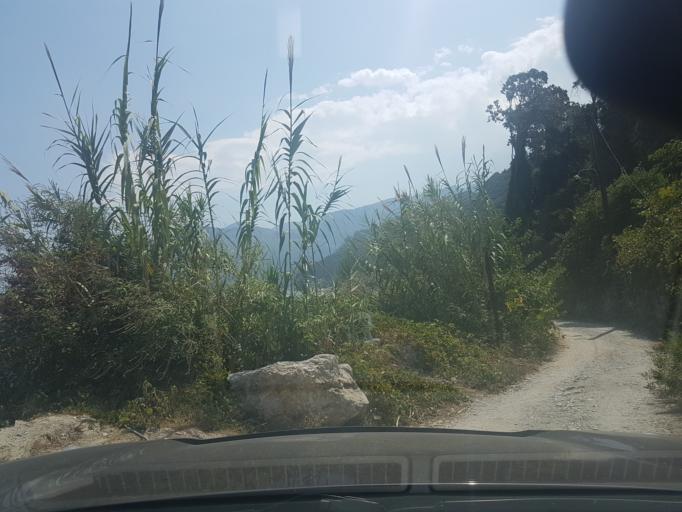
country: GR
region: Central Greece
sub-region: Nomos Evvoias
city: Kymi
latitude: 38.6716
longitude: 23.9184
